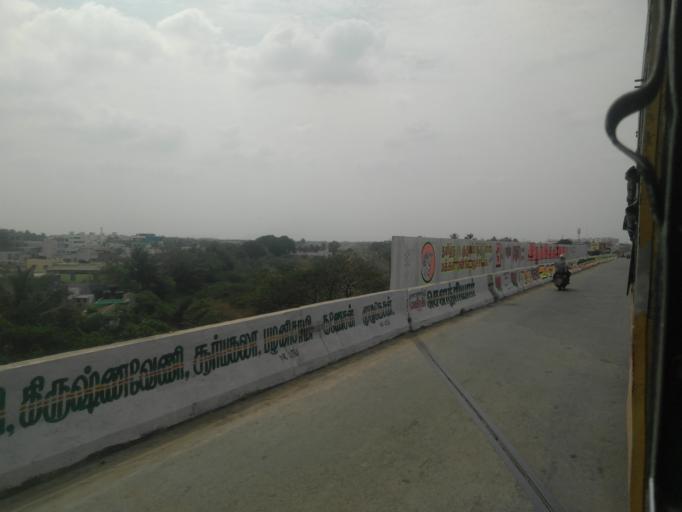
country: IN
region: Tamil Nadu
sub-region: Coimbatore
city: Irugur
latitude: 11.0022
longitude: 77.0546
